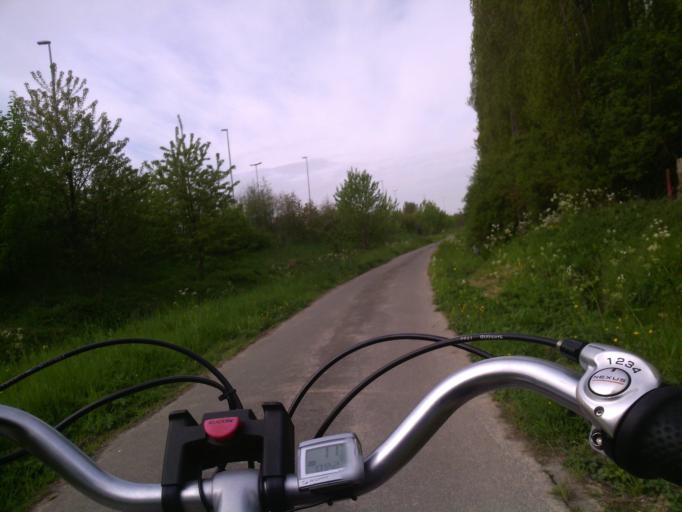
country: BE
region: Wallonia
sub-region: Province du Hainaut
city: Mouscron
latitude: 50.7702
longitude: 3.1877
